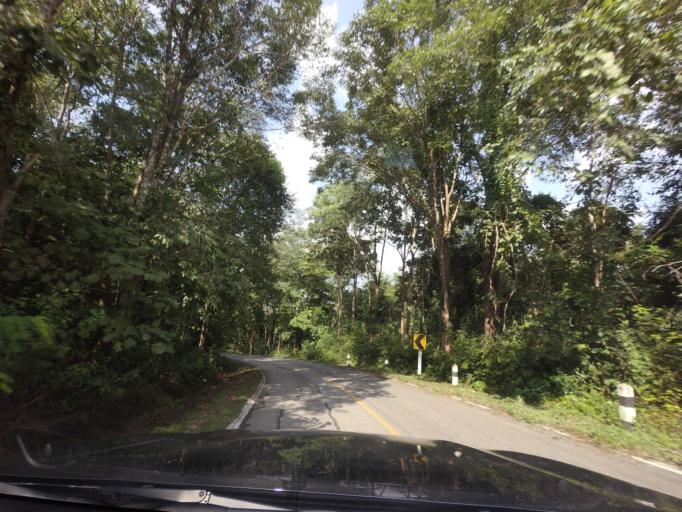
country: TH
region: Uttaradit
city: Ban Khok
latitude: 18.1745
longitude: 101.0757
